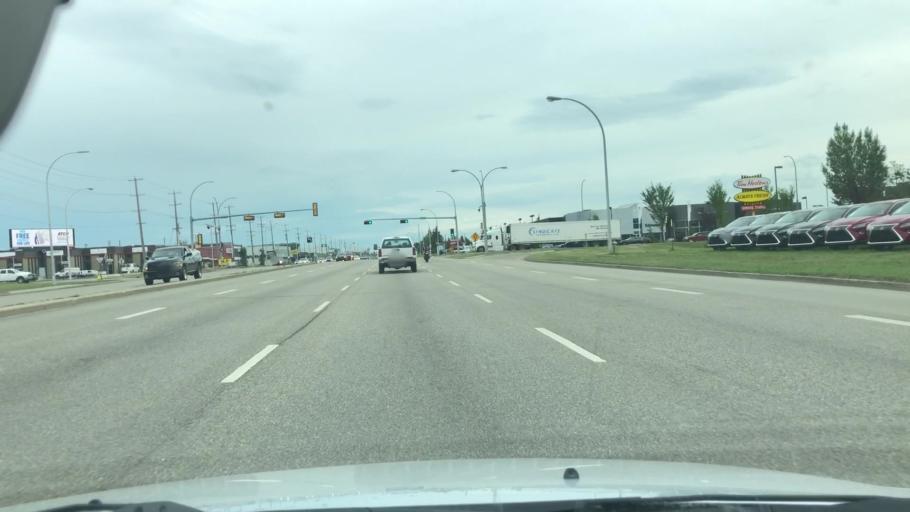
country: CA
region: Alberta
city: St. Albert
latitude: 53.5606
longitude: -113.6154
